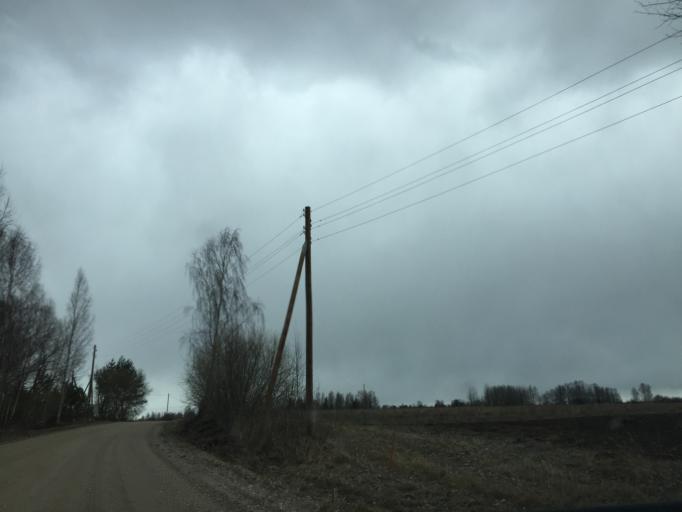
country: LV
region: Varkava
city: Vecvarkava
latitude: 56.0716
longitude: 26.5324
